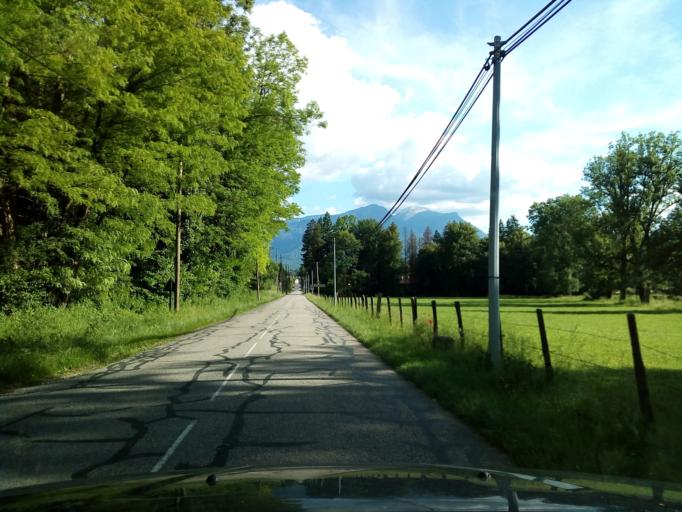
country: FR
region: Rhone-Alpes
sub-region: Departement de la Savoie
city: Les Echelles
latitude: 45.4435
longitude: 5.7531
